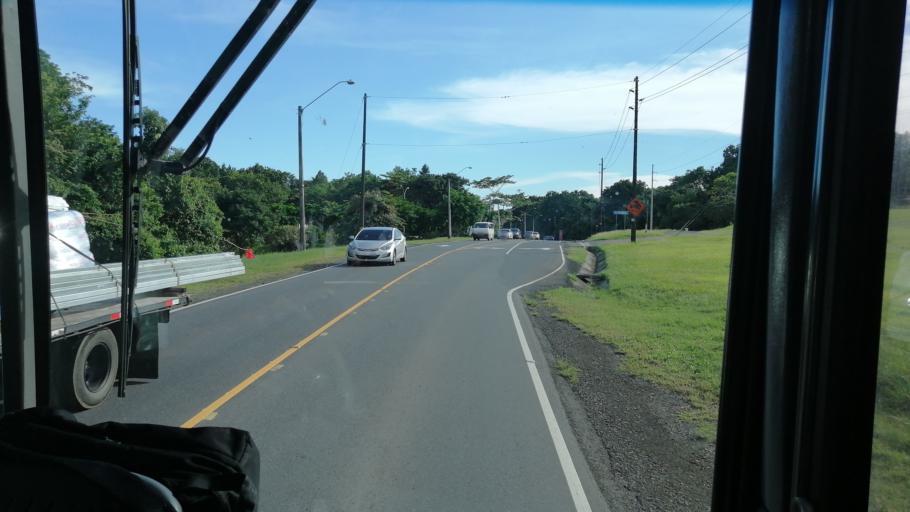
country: PA
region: Panama
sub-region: Distrito de Panama
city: Ancon
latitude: 8.9328
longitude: -79.5911
